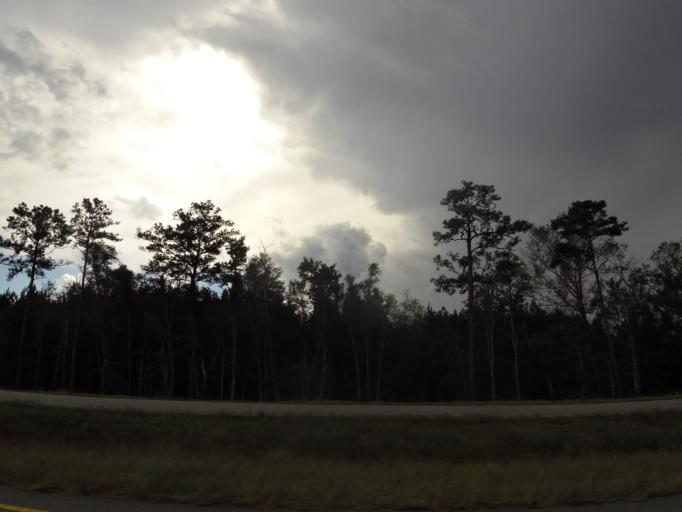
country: US
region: Georgia
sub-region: Glynn County
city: Dock Junction
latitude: 31.3430
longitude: -81.6035
